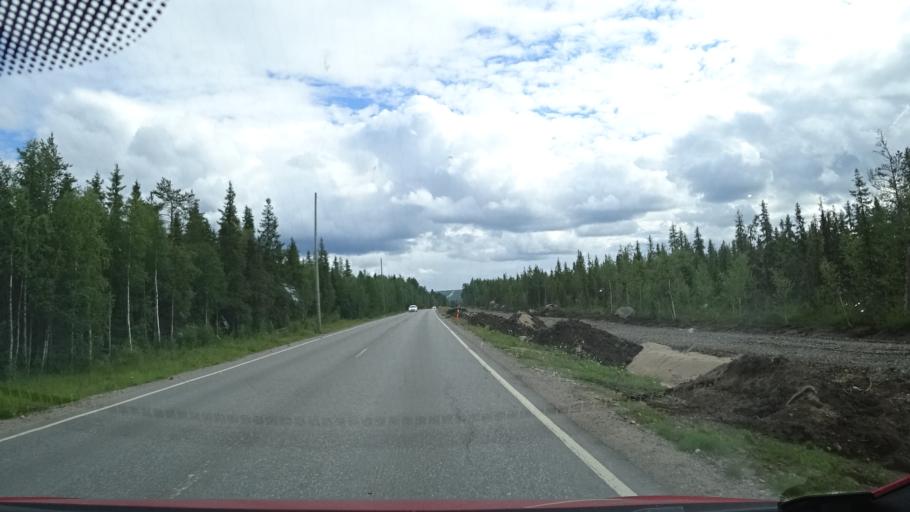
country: FI
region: Lapland
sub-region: Rovaniemi
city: Rovaniemi
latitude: 66.5357
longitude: 25.7283
